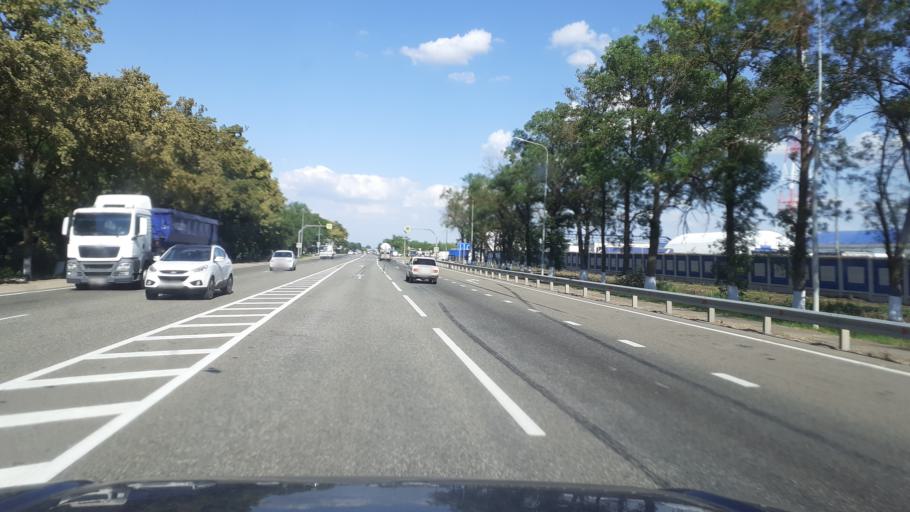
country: RU
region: Krasnodarskiy
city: Afipskiy
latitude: 44.8827
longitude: 38.7878
